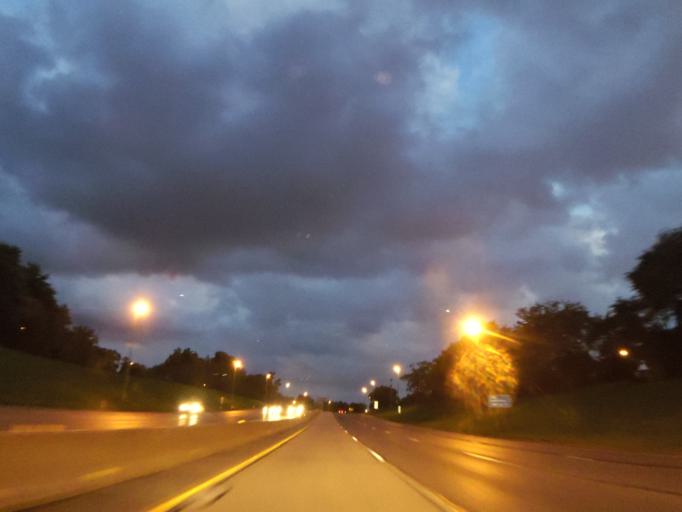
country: US
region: Illinois
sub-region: Saint Clair County
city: Cahokia
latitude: 38.5691
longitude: -90.2391
